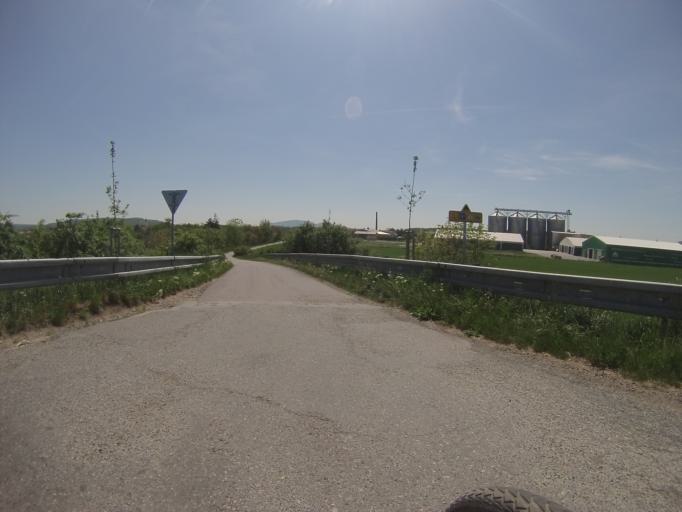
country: CZ
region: South Moravian
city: Vranovice
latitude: 48.9712
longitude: 16.6003
